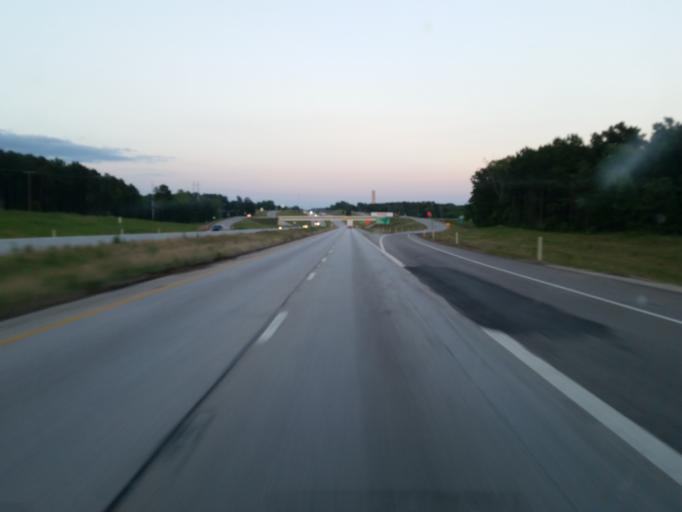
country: US
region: Texas
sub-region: Smith County
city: Hideaway
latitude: 32.4692
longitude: -95.4434
